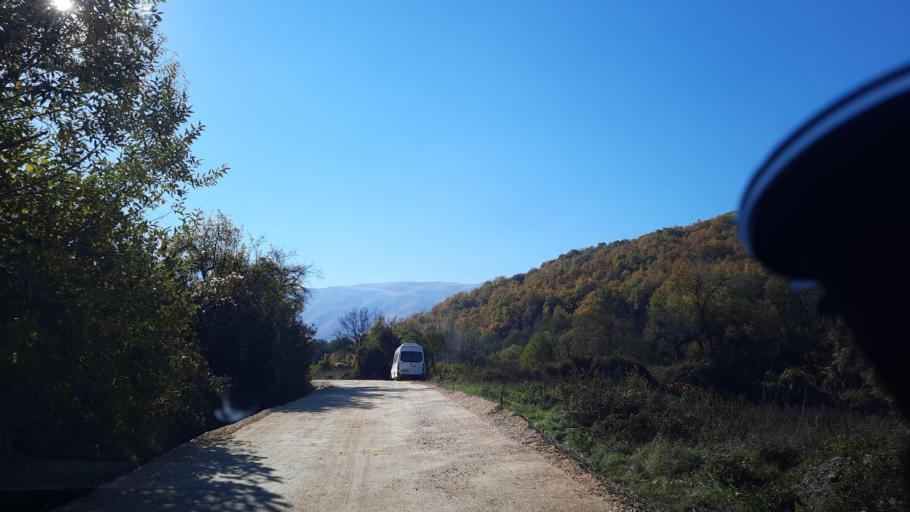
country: MK
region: Demir Hisar
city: Sopotnica
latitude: 41.2724
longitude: 21.0869
